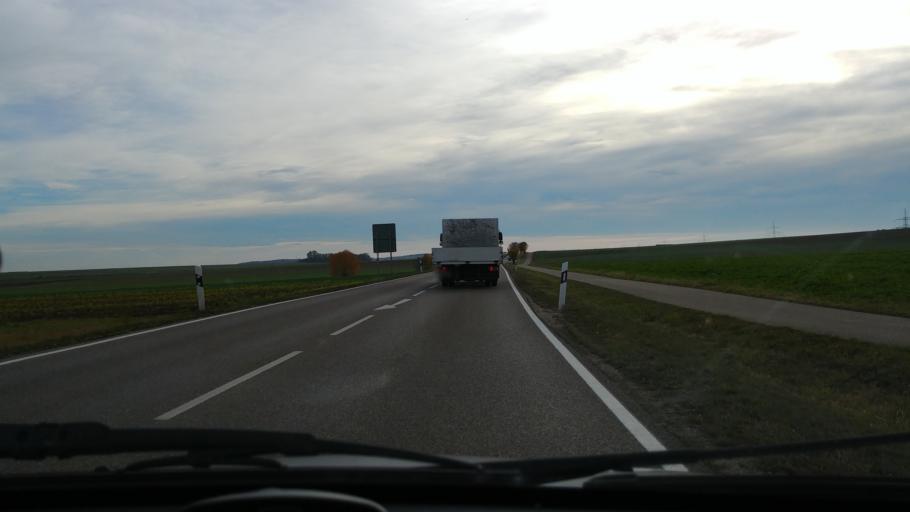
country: DE
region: Bavaria
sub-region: Swabia
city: Bachhagel
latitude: 48.6362
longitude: 10.2955
